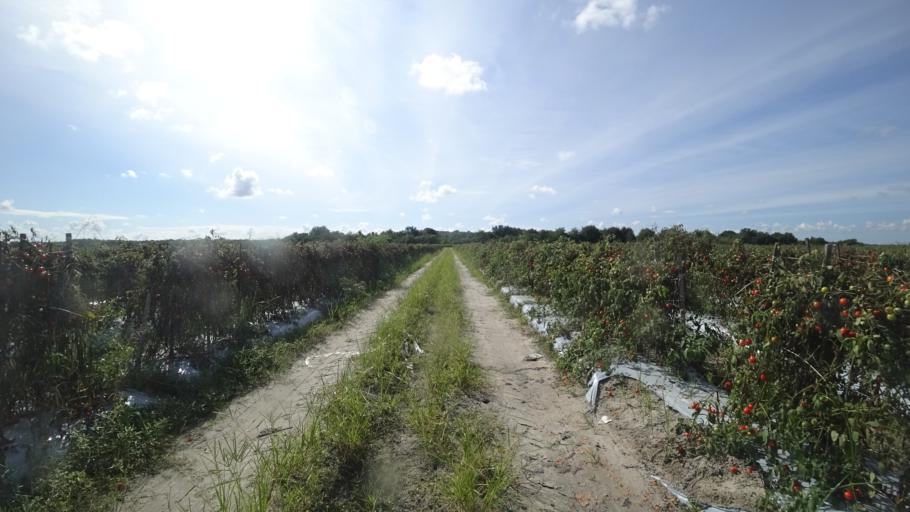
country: US
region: Florida
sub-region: Sarasota County
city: The Meadows
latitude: 27.4452
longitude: -82.3119
